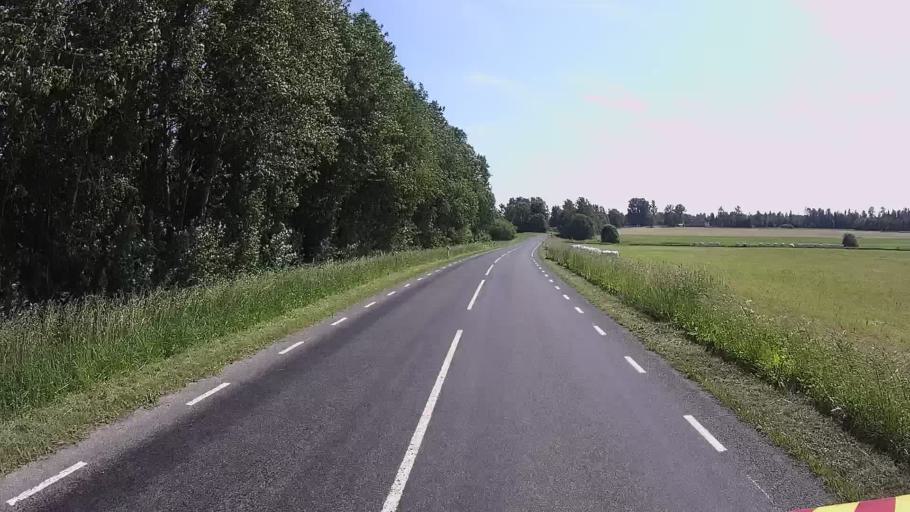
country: EE
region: Viljandimaa
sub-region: Karksi vald
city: Karksi-Nuia
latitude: 58.0628
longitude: 25.5501
